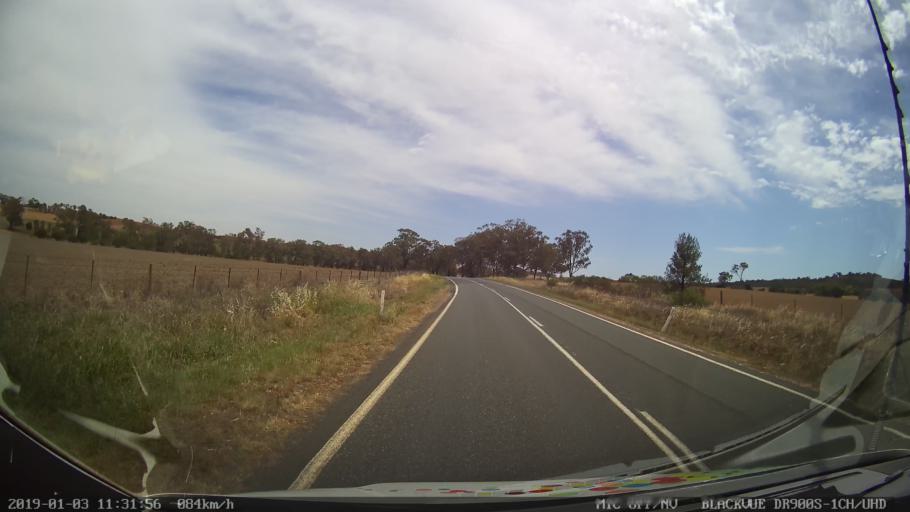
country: AU
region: New South Wales
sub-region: Weddin
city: Grenfell
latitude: -33.9644
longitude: 148.1811
